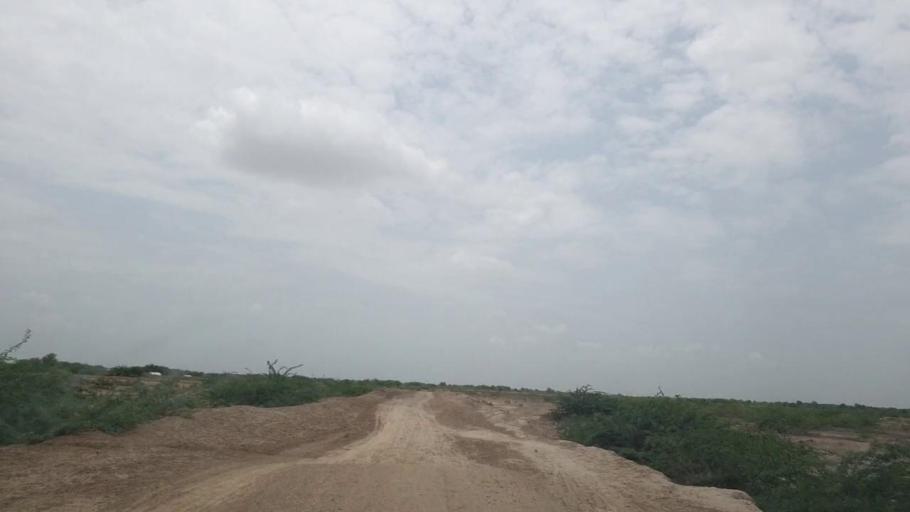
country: PK
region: Sindh
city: Digri
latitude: 24.9242
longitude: 69.1698
